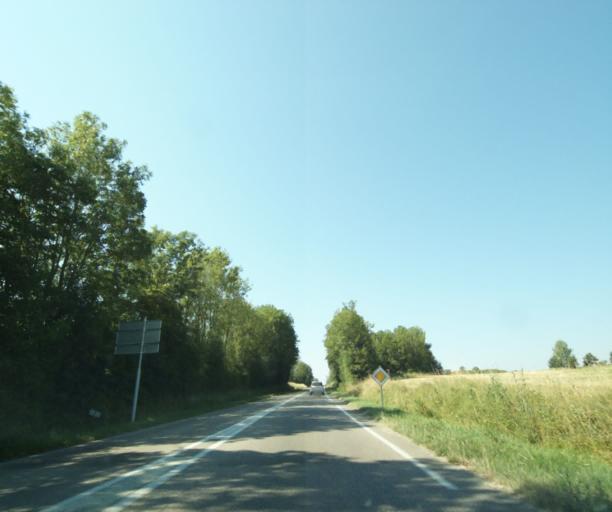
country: FR
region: Lorraine
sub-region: Departement de Meurthe-et-Moselle
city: Toul
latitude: 48.6603
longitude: 5.8771
